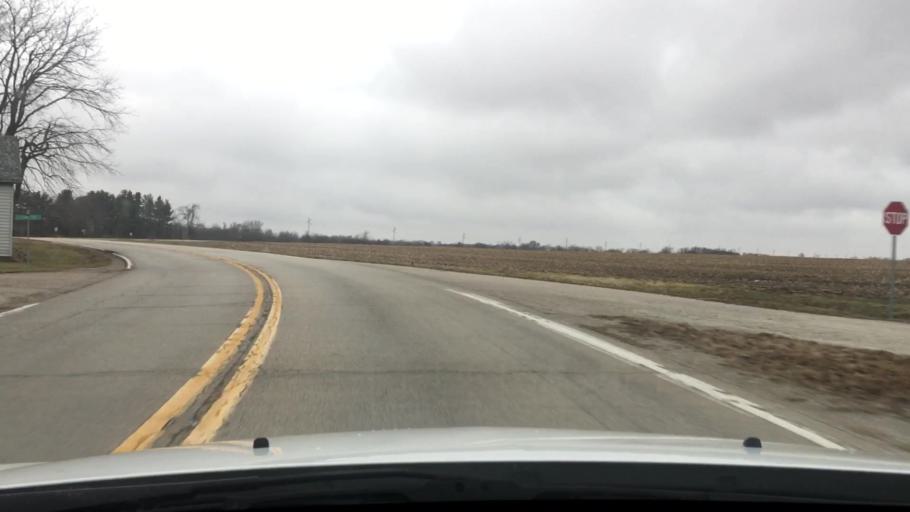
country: US
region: Illinois
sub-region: Iroquois County
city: Sheldon
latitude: 40.8291
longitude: -87.5827
